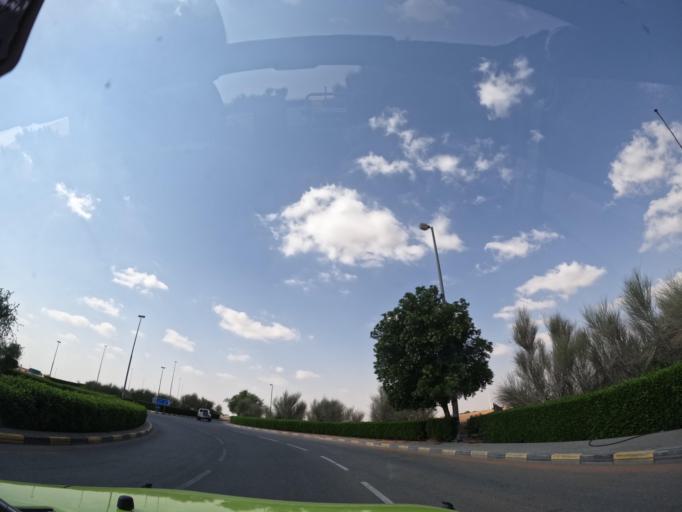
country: AE
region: Ash Shariqah
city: Adh Dhayd
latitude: 24.9650
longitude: 55.7062
